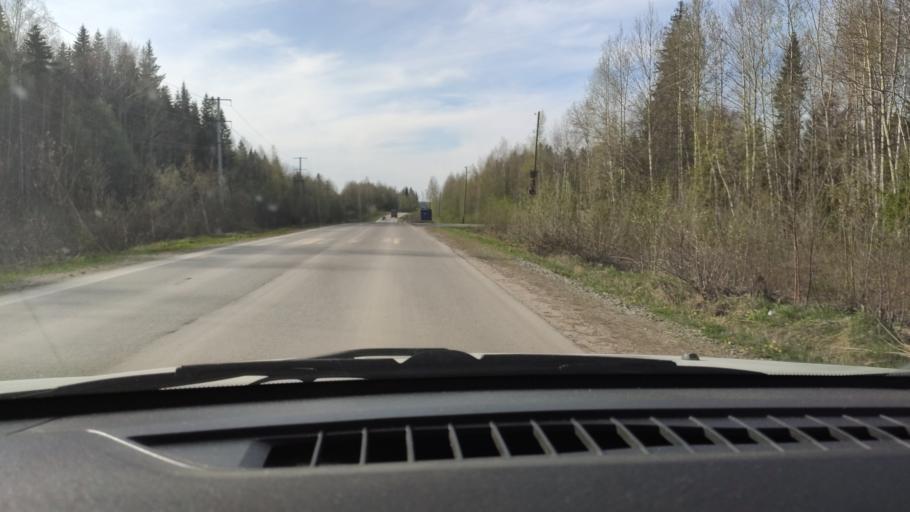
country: RU
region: Perm
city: Novyye Lyady
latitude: 57.9283
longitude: 56.6500
